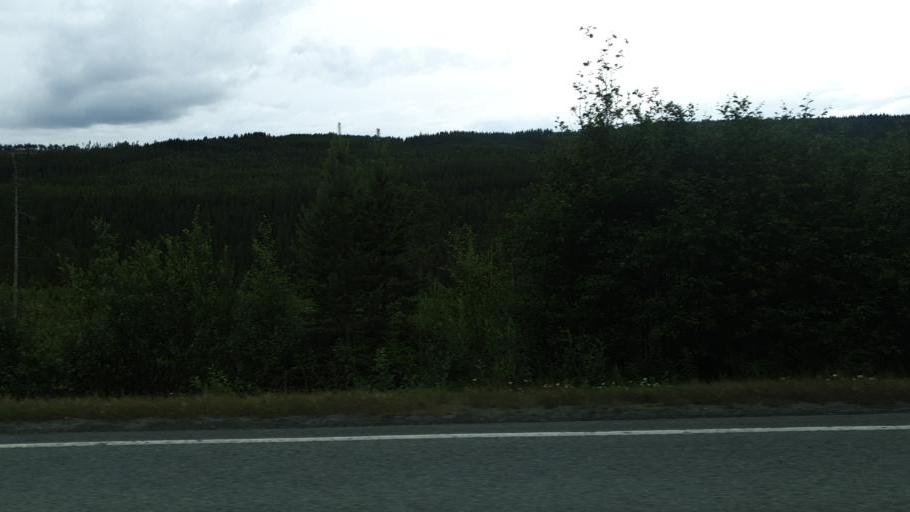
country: NO
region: Sor-Trondelag
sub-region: Rennebu
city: Berkak
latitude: 62.7405
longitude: 9.9792
